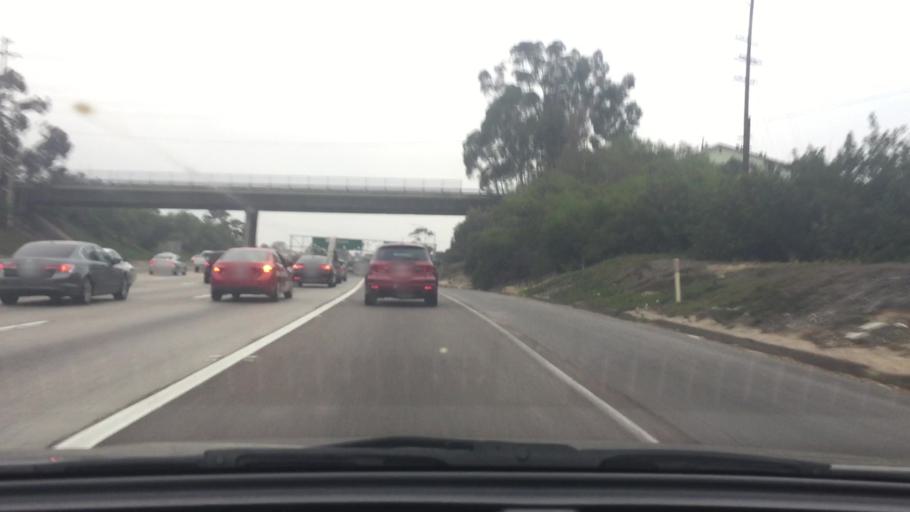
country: US
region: California
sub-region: San Diego County
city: National City
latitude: 32.7294
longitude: -117.1065
